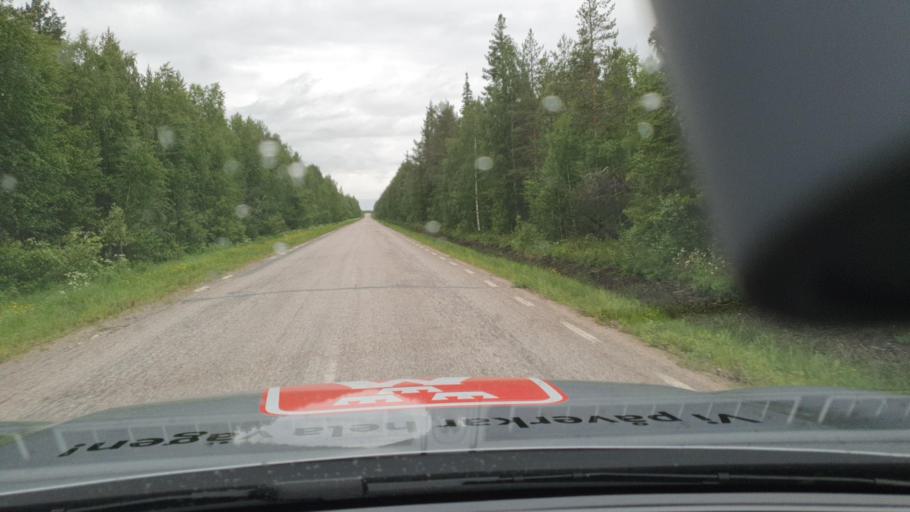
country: SE
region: Norrbotten
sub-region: Overkalix Kommun
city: OEverkalix
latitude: 66.3677
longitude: 22.8019
